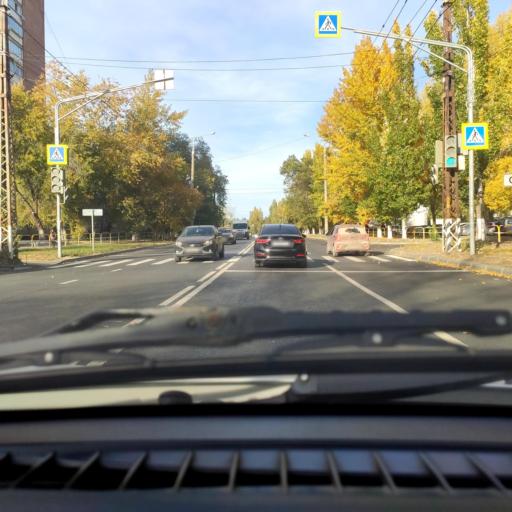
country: RU
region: Samara
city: Zhigulevsk
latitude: 53.4805
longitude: 49.4594
